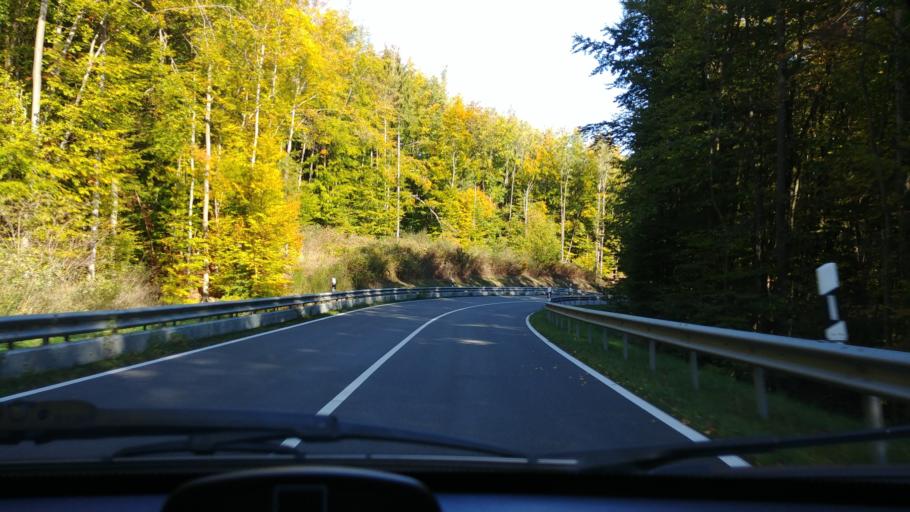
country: DE
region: Rheinland-Pfalz
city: Mudershausen
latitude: 50.2816
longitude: 8.0263
